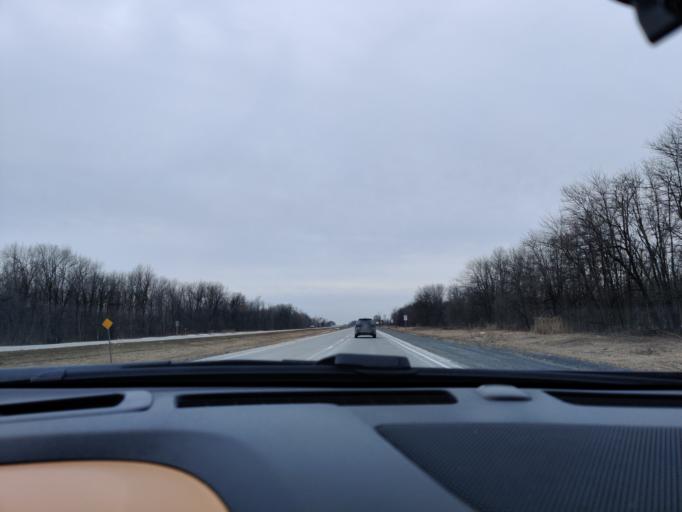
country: US
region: New York
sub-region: St. Lawrence County
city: Massena
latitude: 45.0455
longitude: -74.9110
